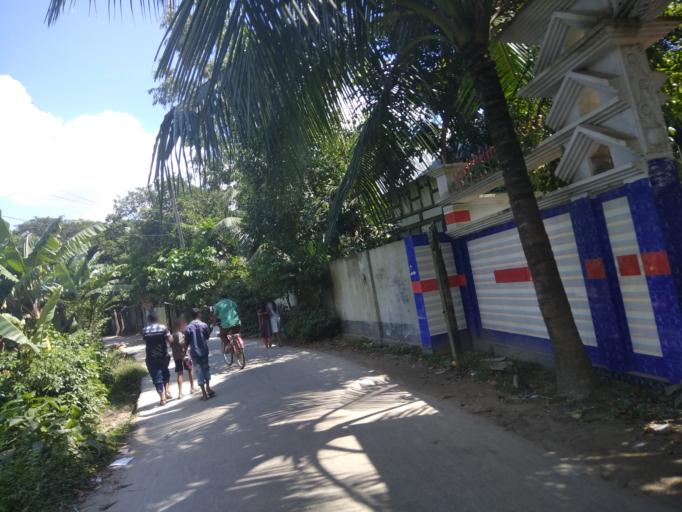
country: BD
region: Dhaka
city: Narayanganj
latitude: 23.4401
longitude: 90.4817
